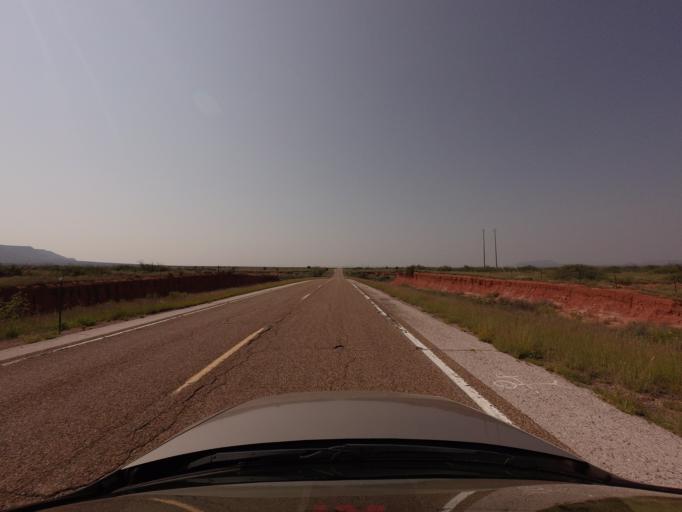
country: US
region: New Mexico
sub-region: Quay County
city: Tucumcari
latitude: 35.0130
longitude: -103.7399
